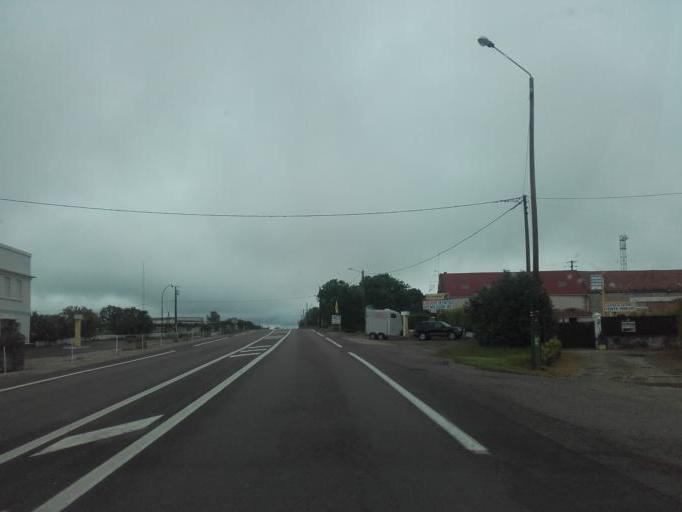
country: FR
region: Bourgogne
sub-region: Departement de la Cote-d'Or
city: Nolay
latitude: 46.9786
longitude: 4.6728
